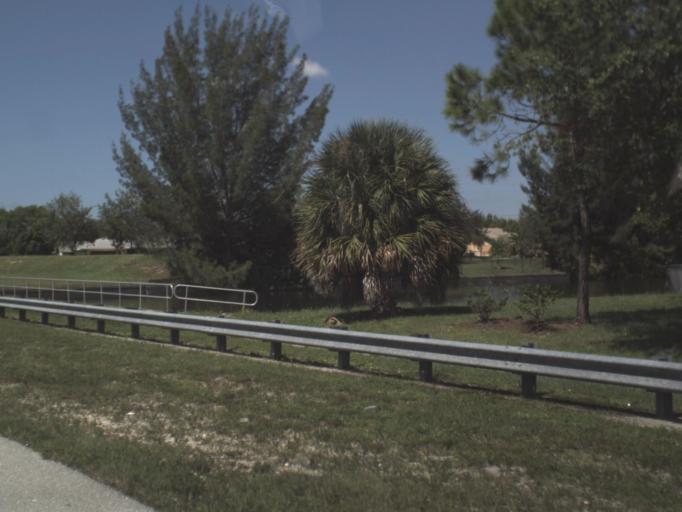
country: US
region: Florida
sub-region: Lee County
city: Cape Coral
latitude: 26.6045
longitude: -81.9645
